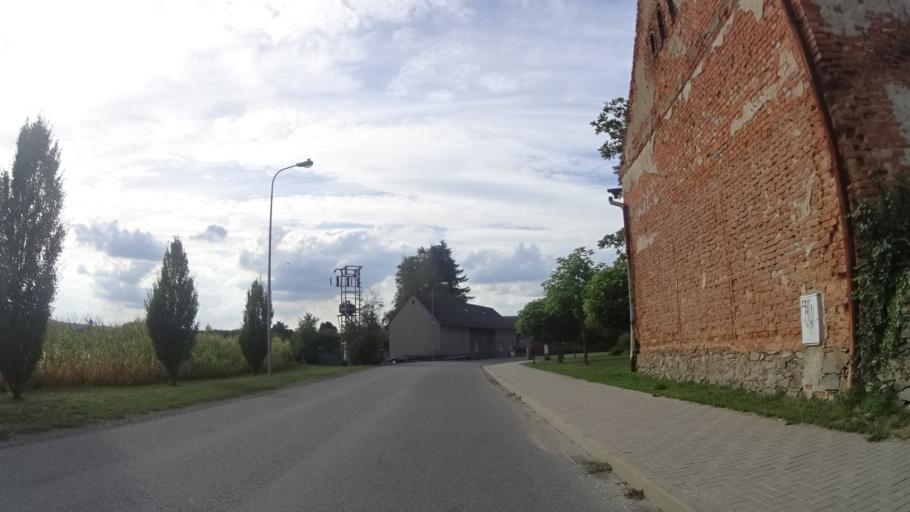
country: CZ
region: Olomoucky
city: Dubicko
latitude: 49.7937
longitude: 16.9651
